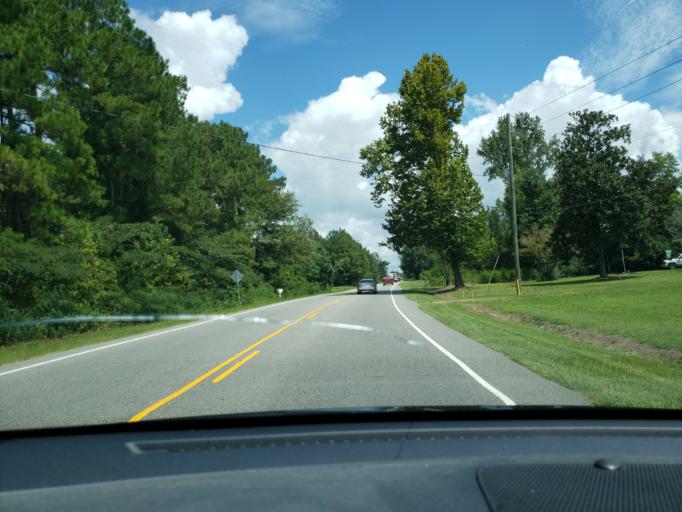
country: US
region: North Carolina
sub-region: Columbus County
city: Brunswick
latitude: 34.2498
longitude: -78.7537
